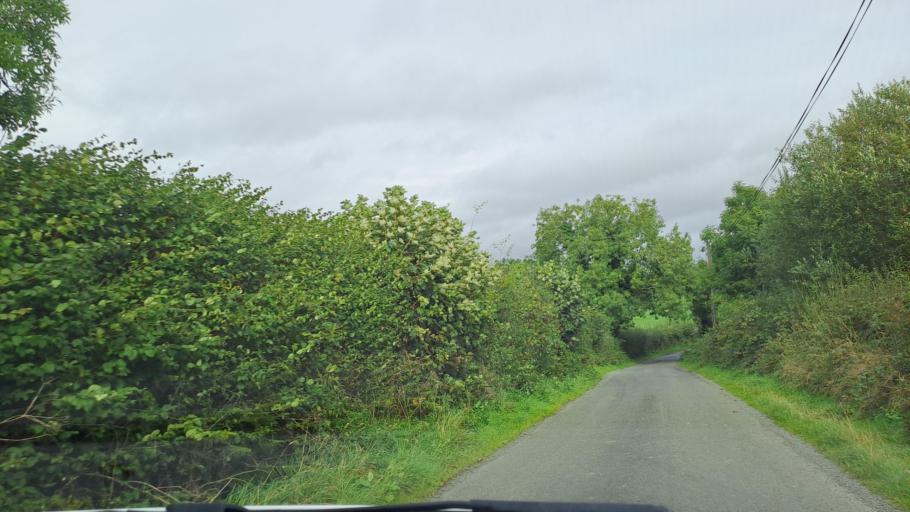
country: IE
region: Ulster
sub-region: An Cabhan
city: Bailieborough
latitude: 54.0094
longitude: -6.9467
